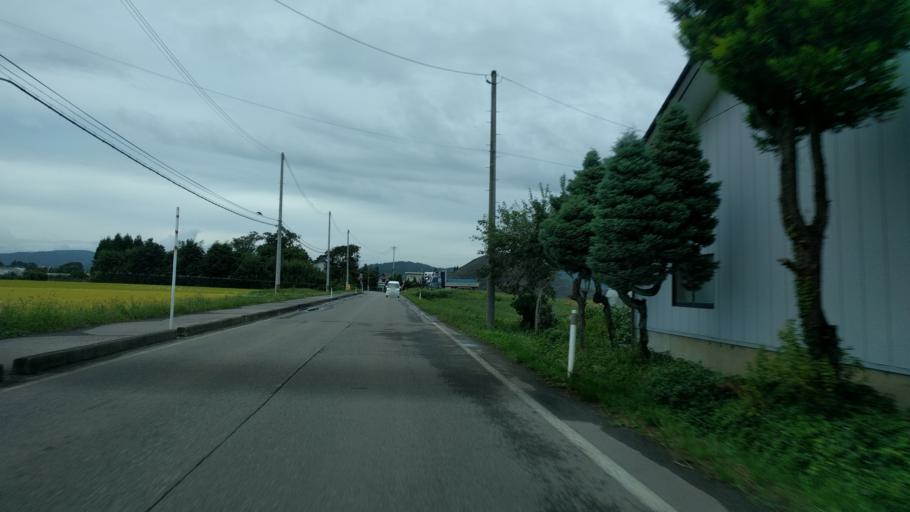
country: JP
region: Fukushima
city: Kitakata
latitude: 37.6097
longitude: 139.8627
